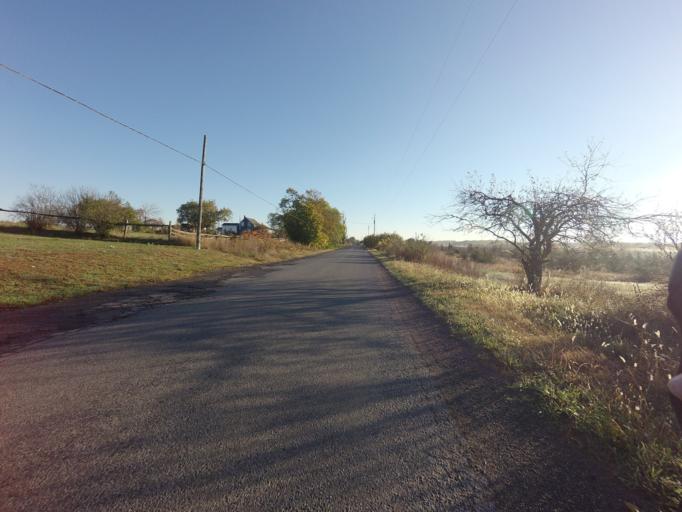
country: CA
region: Ontario
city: Quinte West
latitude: 44.0186
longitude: -77.4988
